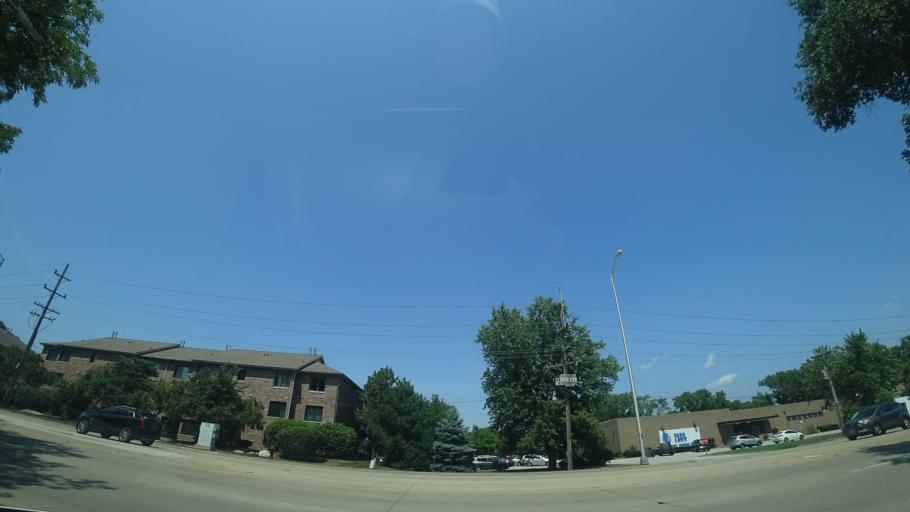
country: US
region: Illinois
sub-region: Cook County
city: Oak Lawn
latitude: 41.6907
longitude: -87.7477
